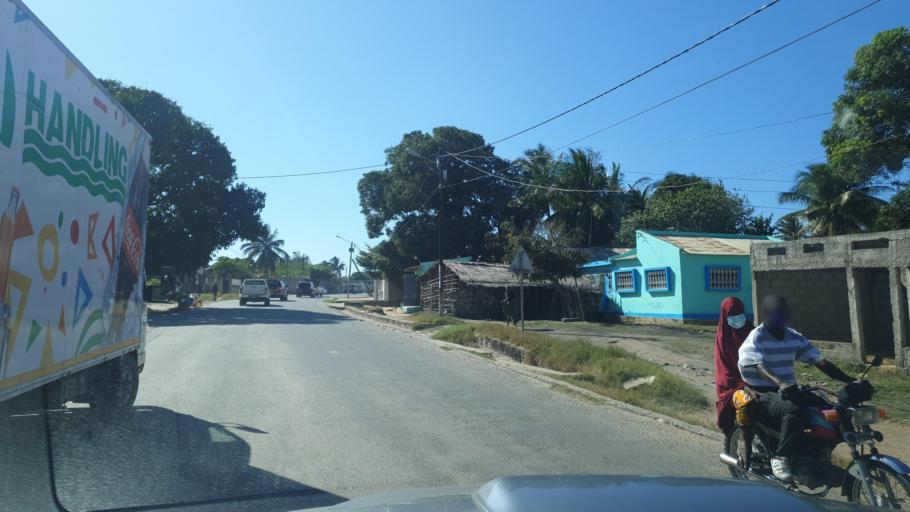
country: MZ
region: Nampula
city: Nacala
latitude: -14.5387
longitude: 40.6825
